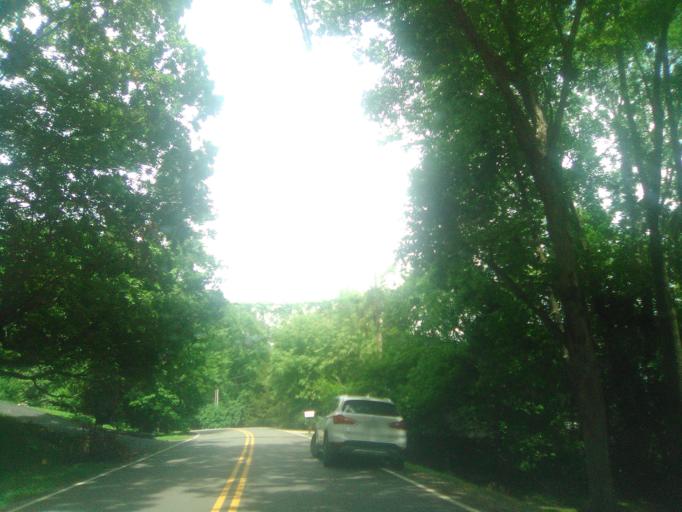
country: US
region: Tennessee
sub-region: Davidson County
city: Forest Hills
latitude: 36.0661
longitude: -86.8499
